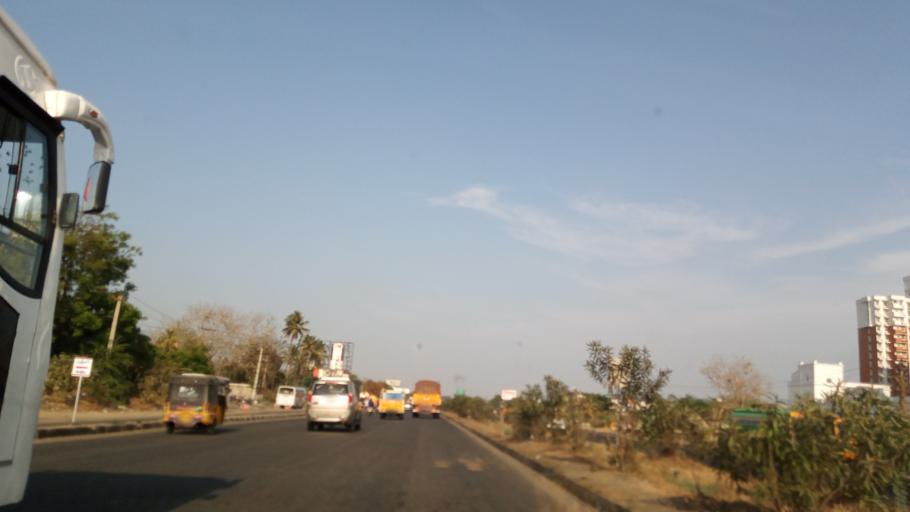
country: IN
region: Tamil Nadu
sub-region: Kancheepuram
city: Poonamalle
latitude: 13.0572
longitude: 80.1026
